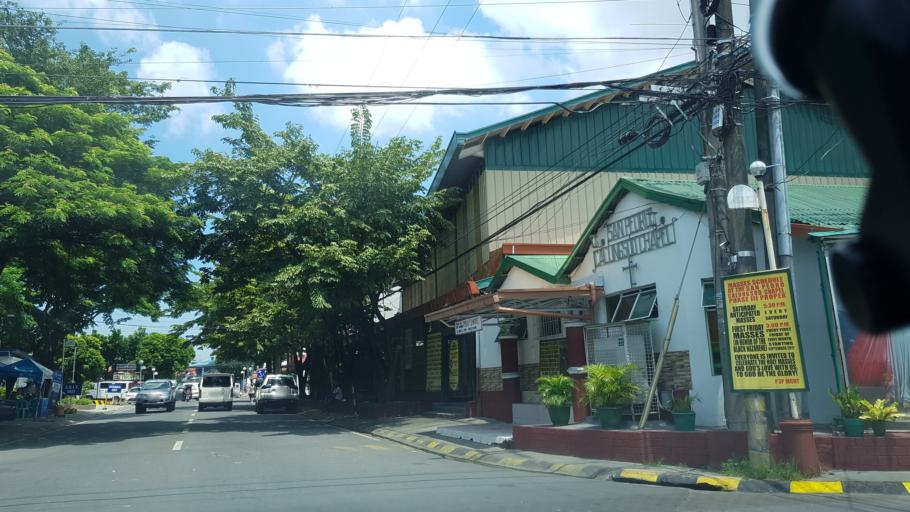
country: PH
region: Calabarzon
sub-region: Province of Rizal
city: Las Pinas
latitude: 14.4387
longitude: 120.9847
